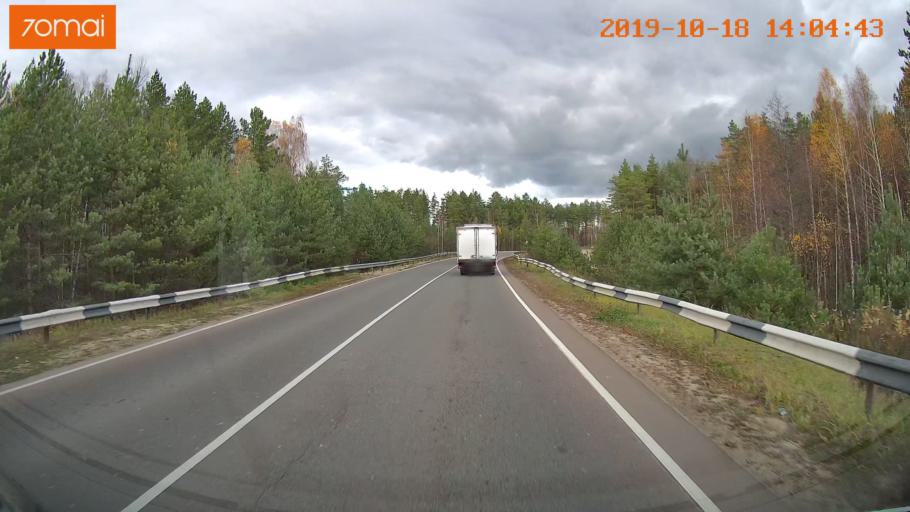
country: RU
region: Rjazan
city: Spas-Klepiki
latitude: 55.1288
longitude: 40.1335
